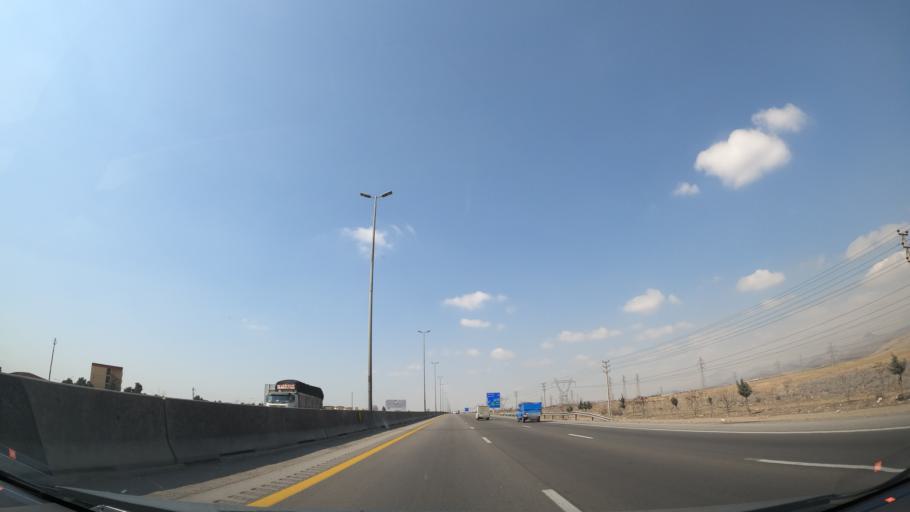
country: IR
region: Qazvin
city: Abyek
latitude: 36.0680
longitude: 50.4838
